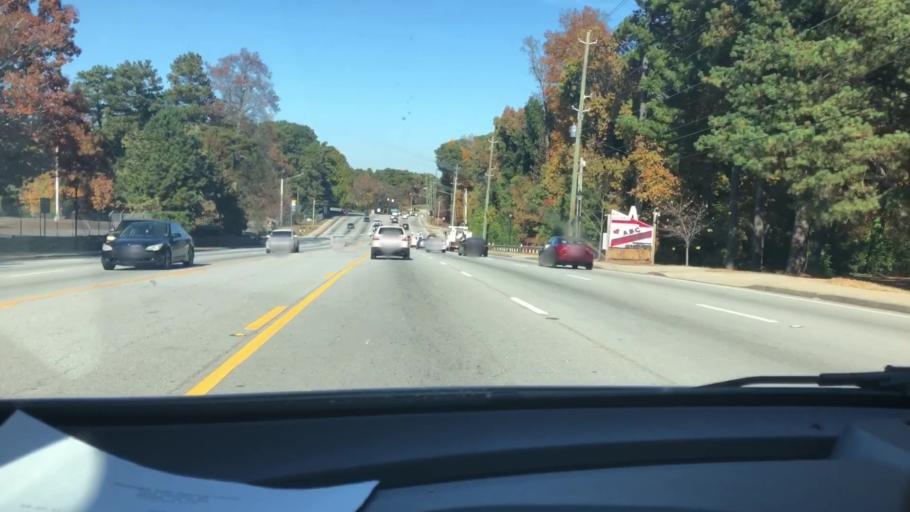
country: US
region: Georgia
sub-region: DeKalb County
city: Avondale Estates
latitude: 33.7706
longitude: -84.2503
